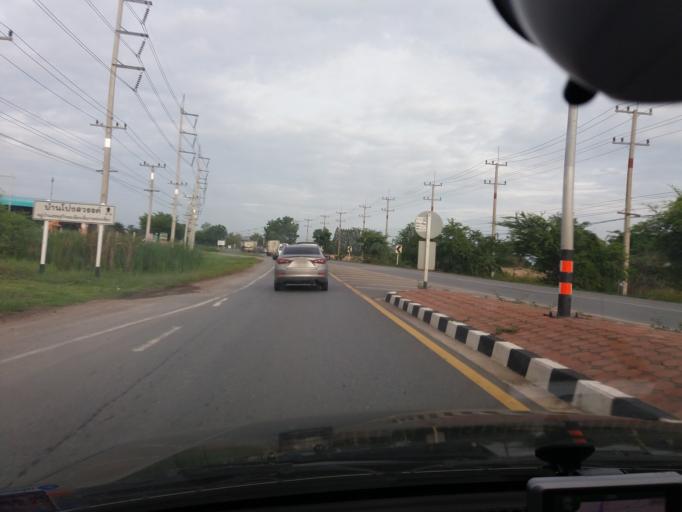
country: TH
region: Kanchanaburi
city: Huai Krachao
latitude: 14.3355
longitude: 99.7548
